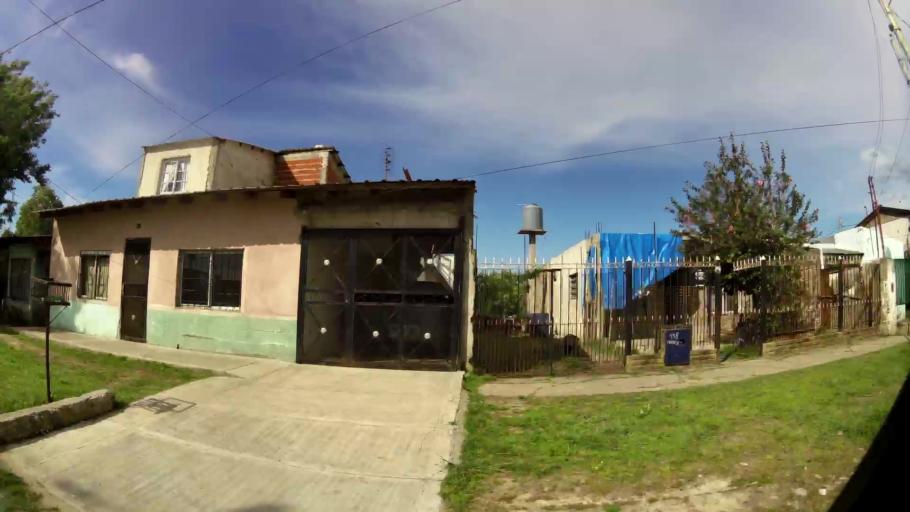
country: AR
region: Buenos Aires
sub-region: Partido de Almirante Brown
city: Adrogue
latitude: -34.8120
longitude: -58.3521
